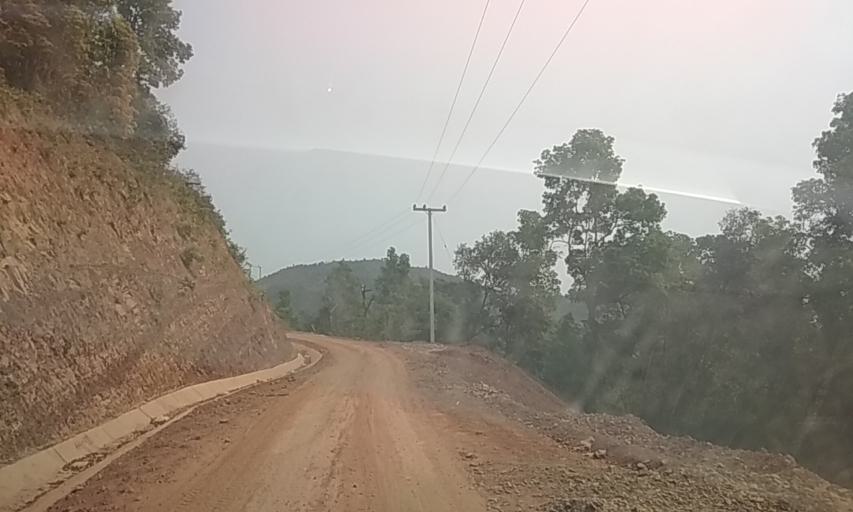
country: VN
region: Huyen Dien Bien
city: Dien Bien Phu
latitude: 21.4712
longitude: 102.7725
